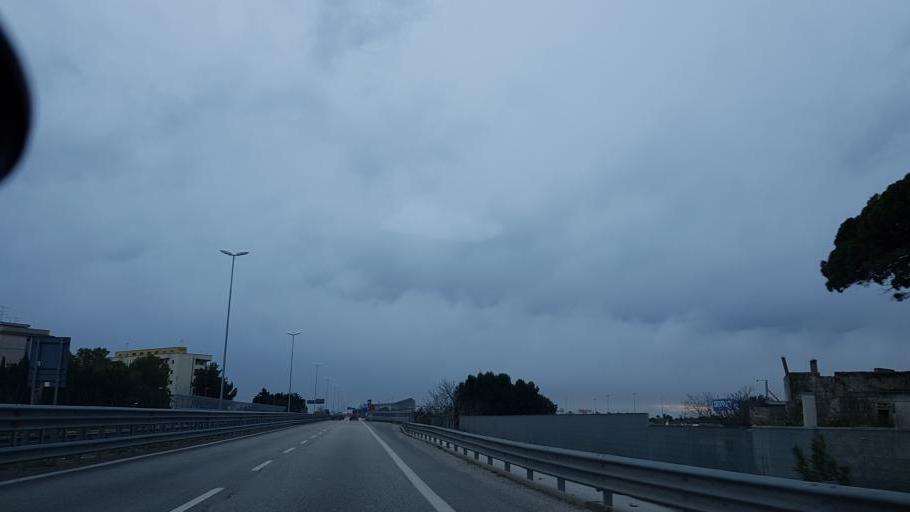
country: IT
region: Apulia
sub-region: Provincia di Brindisi
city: Brindisi
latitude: 40.6228
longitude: 17.9138
